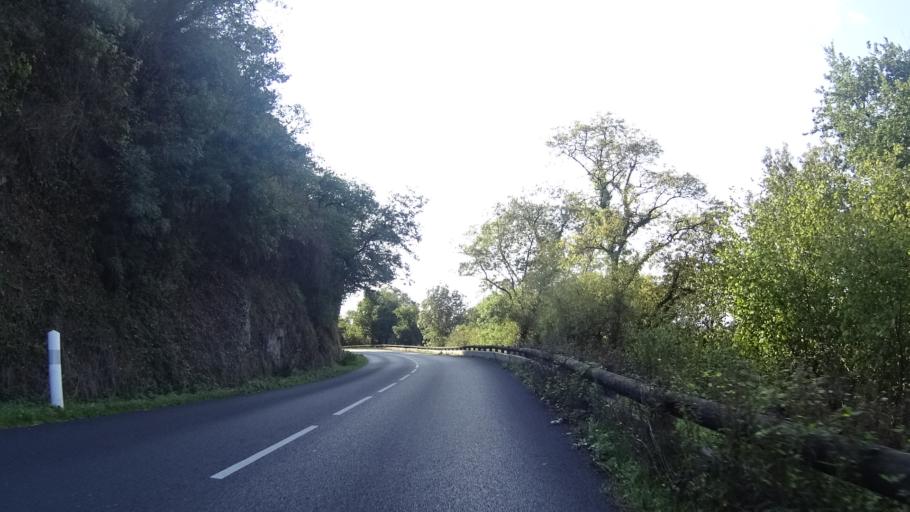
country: FR
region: Pays de la Loire
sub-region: Departement de Maine-et-Loire
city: Rochefort-sur-Loire
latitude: 47.3467
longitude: -0.6787
